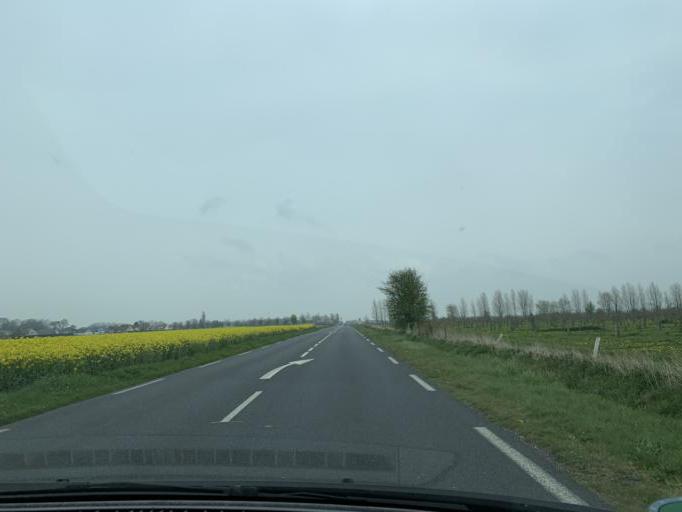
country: FR
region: Haute-Normandie
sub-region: Departement de la Seine-Maritime
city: Martin-Eglise
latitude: 49.9198
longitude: 1.1312
